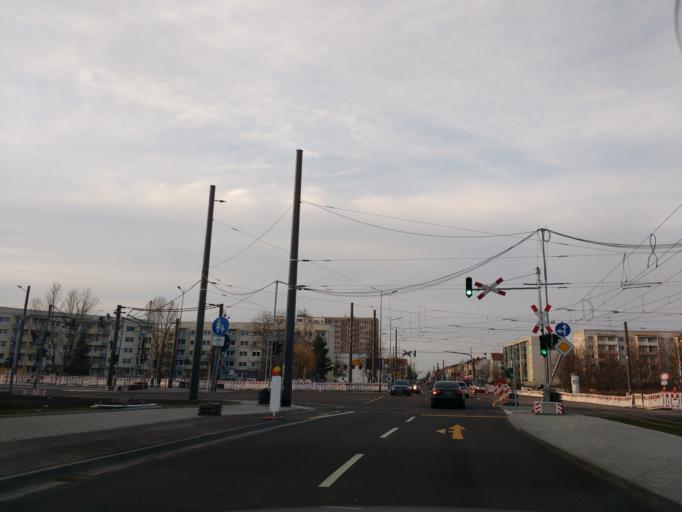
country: DE
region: Saxony-Anhalt
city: Schkopau
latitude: 51.4484
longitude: 11.9604
